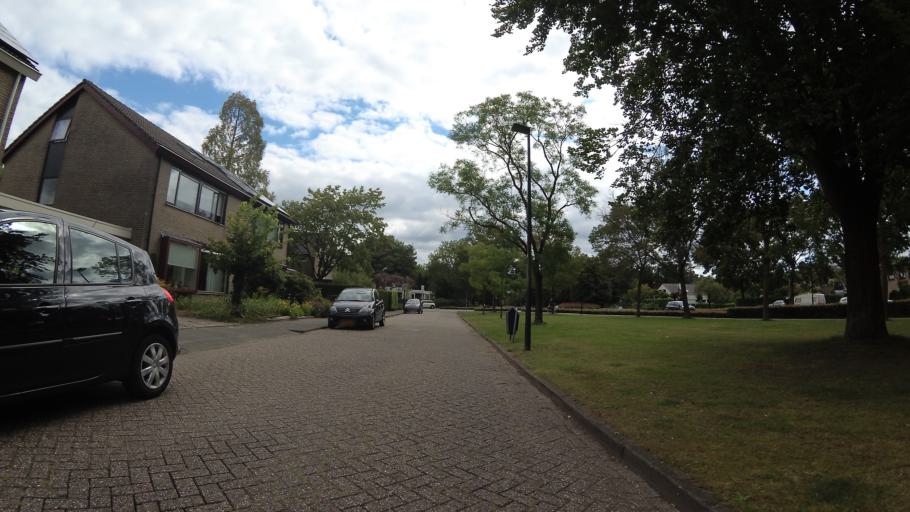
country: NL
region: North Brabant
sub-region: Gemeente Dongen
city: Dongen
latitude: 51.6292
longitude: 4.9290
